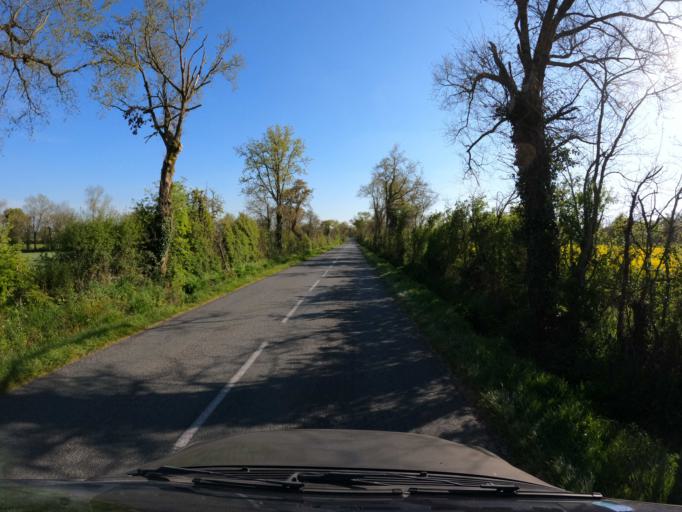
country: FR
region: Pays de la Loire
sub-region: Departement de la Vendee
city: Beaurepaire
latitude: 46.9192
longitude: -1.1220
